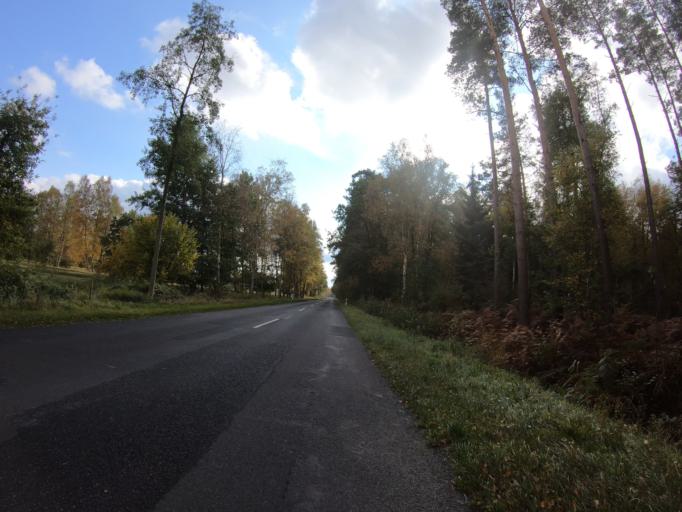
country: DE
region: Lower Saxony
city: Schoneworde
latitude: 52.5957
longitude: 10.6412
